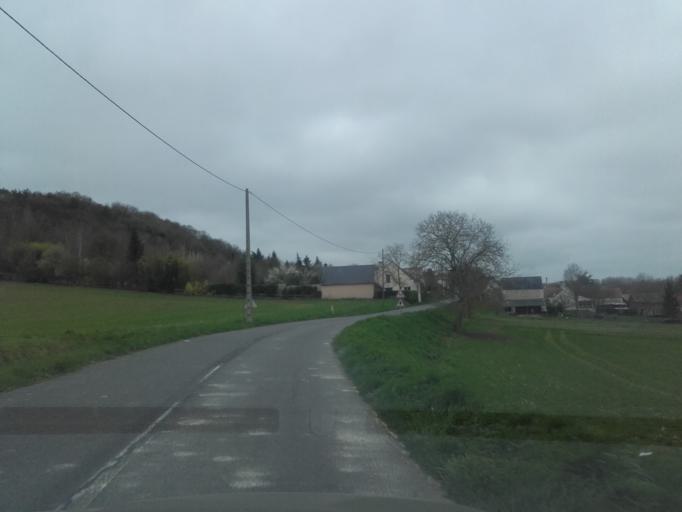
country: FR
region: Centre
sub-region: Departement d'Indre-et-Loire
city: Huismes
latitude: 47.2430
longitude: 0.2584
